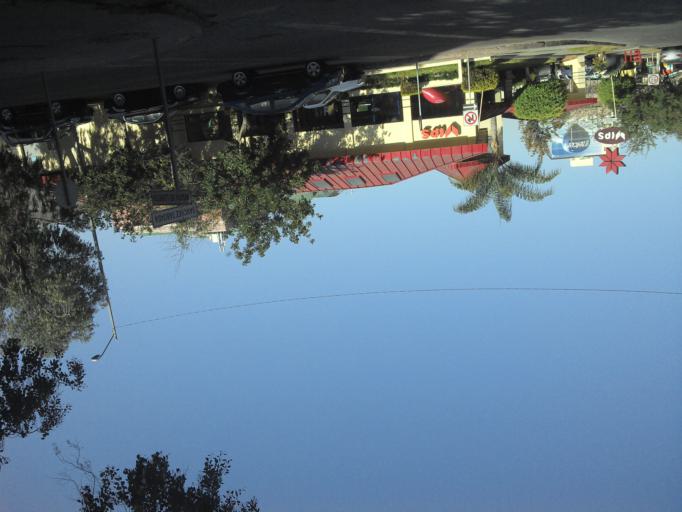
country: MX
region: Baja California
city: Tijuana
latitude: 32.5179
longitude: -117.0093
